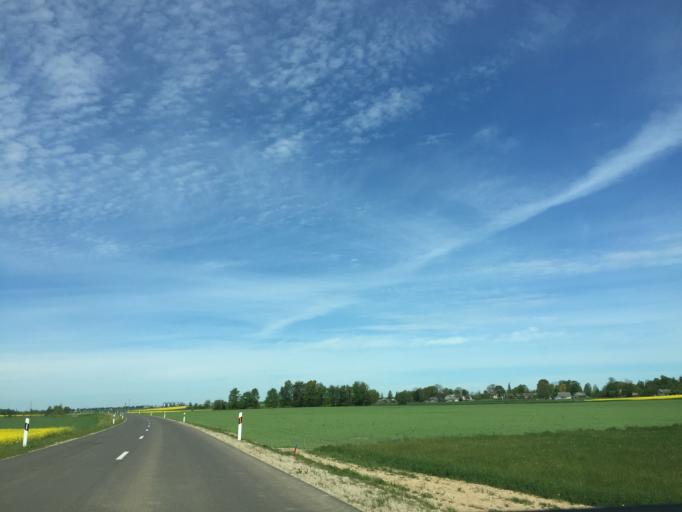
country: LT
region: Panevezys
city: Pasvalys
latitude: 56.1140
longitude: 24.2234
